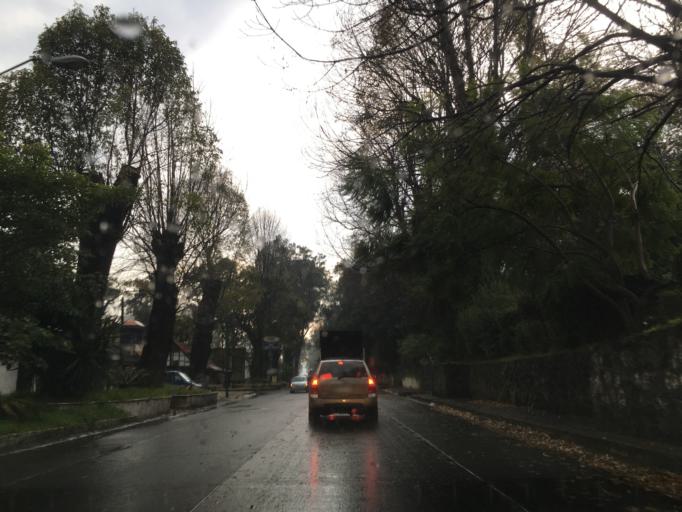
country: MX
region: Michoacan
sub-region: Uruapan
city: Uruapan
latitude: 19.4283
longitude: -102.0728
